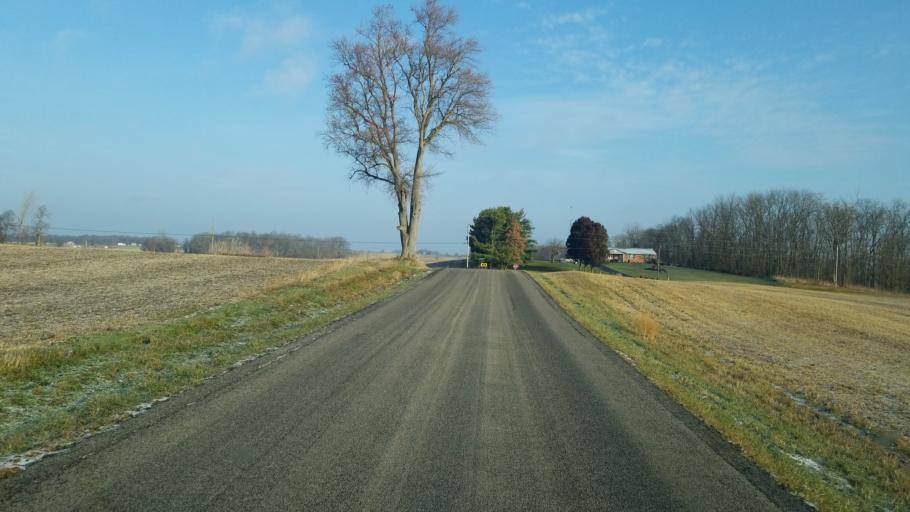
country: US
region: Ohio
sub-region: Crawford County
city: Crestline
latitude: 40.8753
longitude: -82.8273
